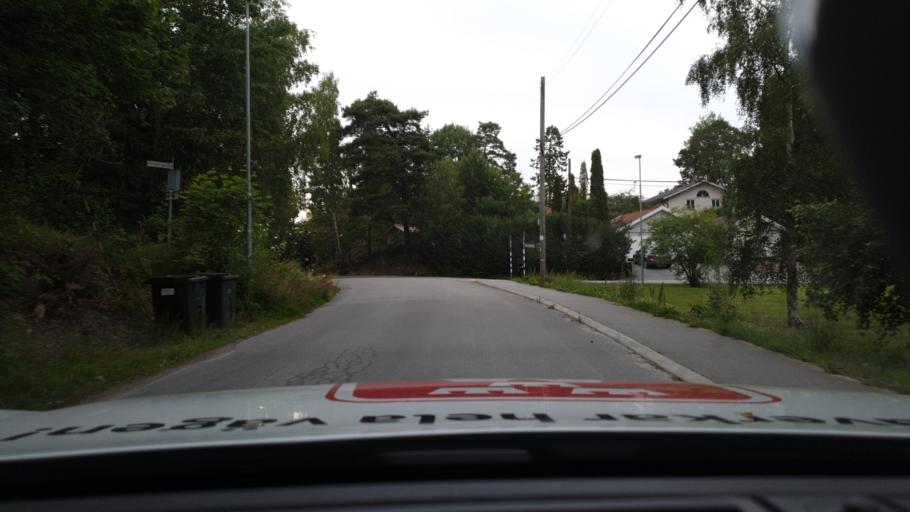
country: SE
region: Stockholm
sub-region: Osterakers Kommun
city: Akersberga
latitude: 59.4589
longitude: 18.3080
